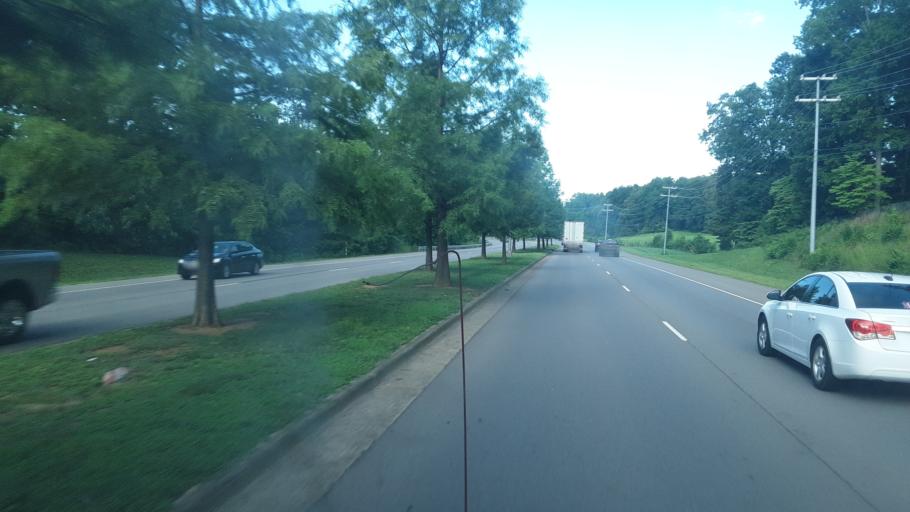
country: US
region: Tennessee
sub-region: Montgomery County
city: Clarksville
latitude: 36.5771
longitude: -87.2806
